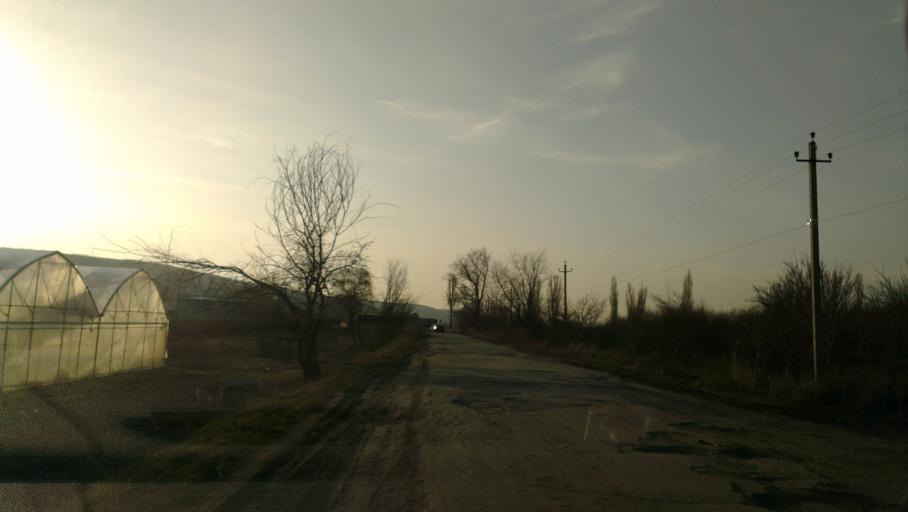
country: MD
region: Laloveni
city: Ialoveni
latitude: 46.9160
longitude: 28.6930
